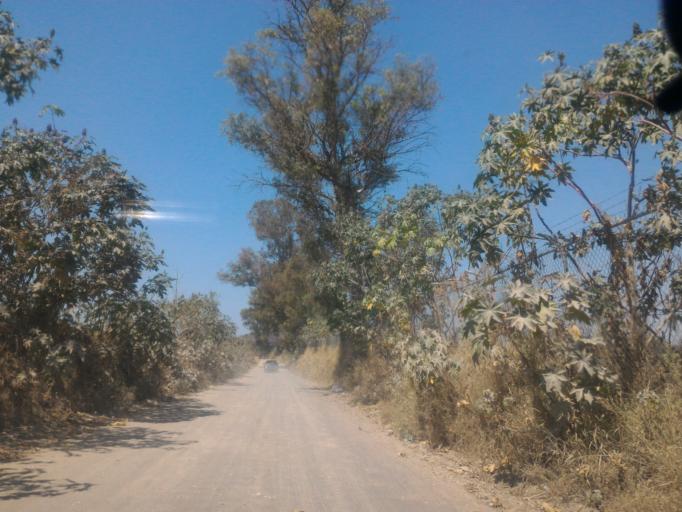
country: MX
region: Jalisco
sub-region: San Pedro Tlaquepaque
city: Paseo del Prado
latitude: 20.5630
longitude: -103.4037
